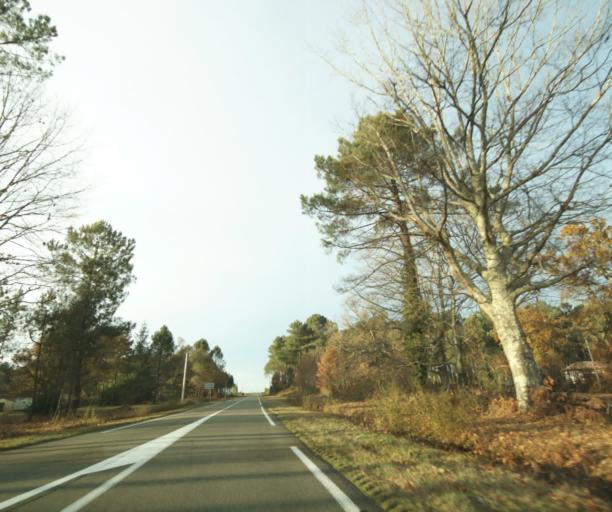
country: FR
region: Aquitaine
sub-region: Departement des Landes
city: Gabarret
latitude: 44.0686
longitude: -0.0604
